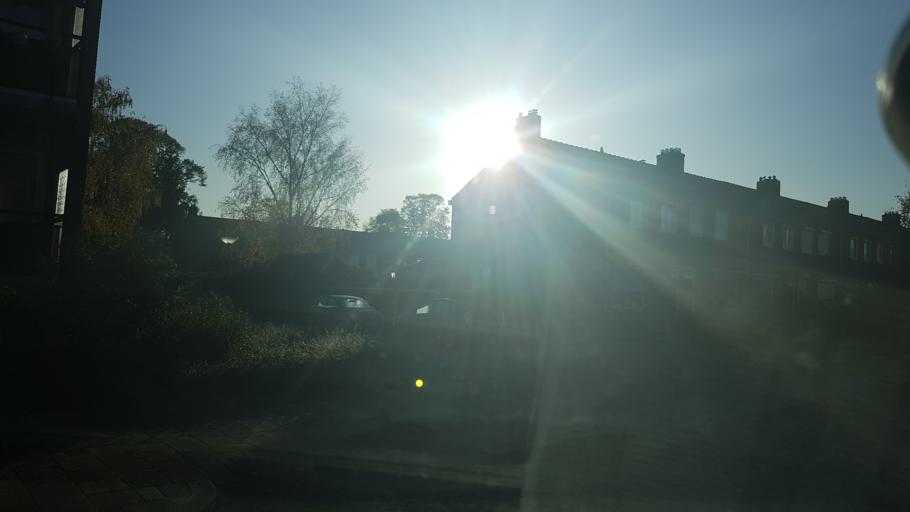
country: NL
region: Gelderland
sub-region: Gemeente Apeldoorn
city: Apeldoorn
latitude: 52.1899
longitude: 5.9673
